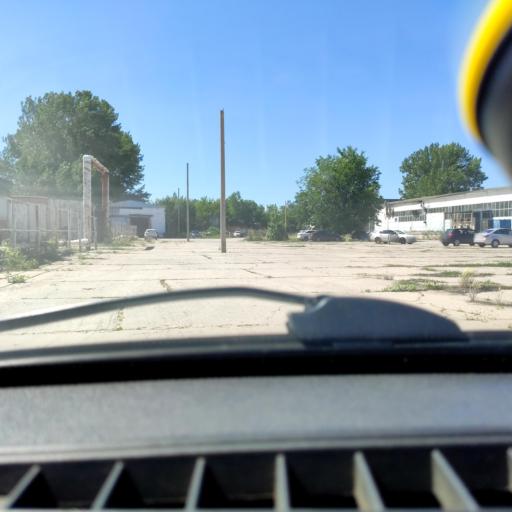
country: RU
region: Samara
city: Tol'yatti
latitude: 53.5720
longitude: 49.3015
